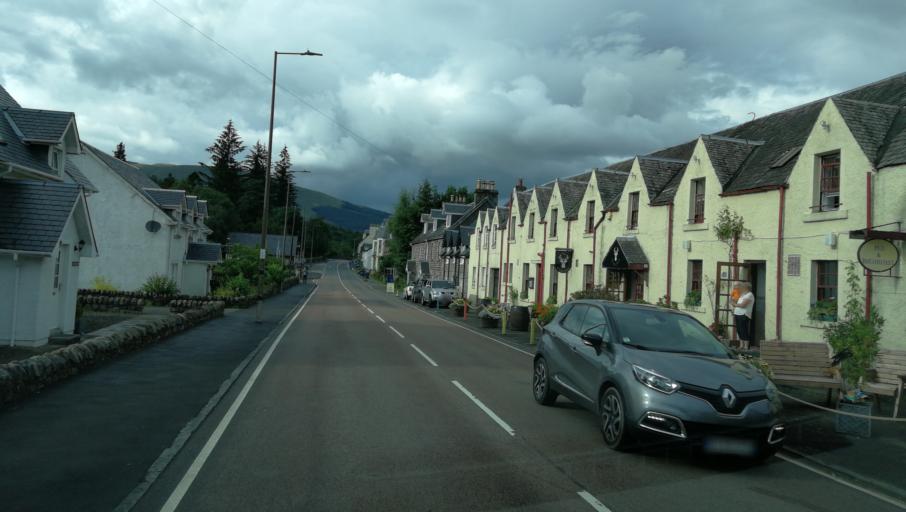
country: GB
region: Scotland
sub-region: Stirling
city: Callander
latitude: 56.3230
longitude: -4.3286
